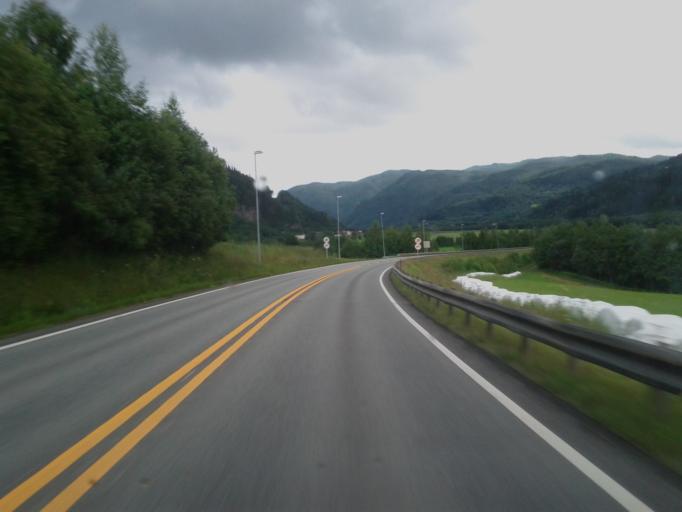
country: NO
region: Sor-Trondelag
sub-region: Melhus
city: Lundamo
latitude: 63.1071
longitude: 10.2356
